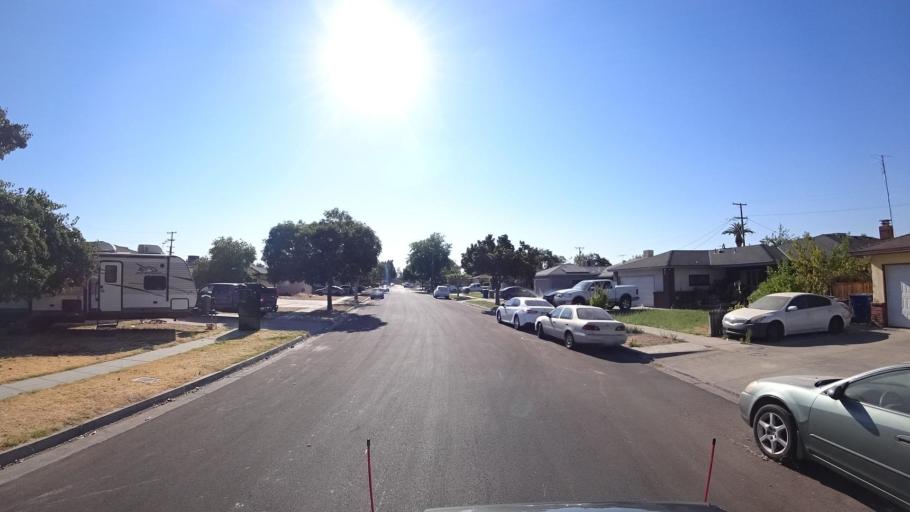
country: US
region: California
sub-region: Fresno County
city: Fresno
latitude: 36.7838
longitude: -119.7604
